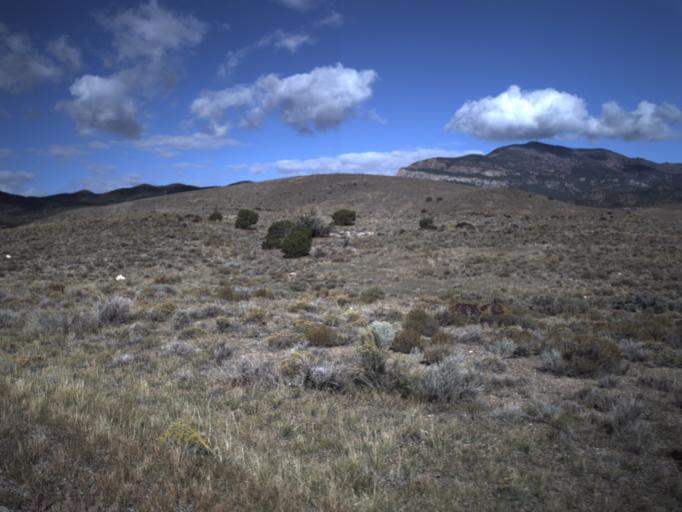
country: US
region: Utah
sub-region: Beaver County
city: Milford
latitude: 38.4570
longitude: -113.2231
